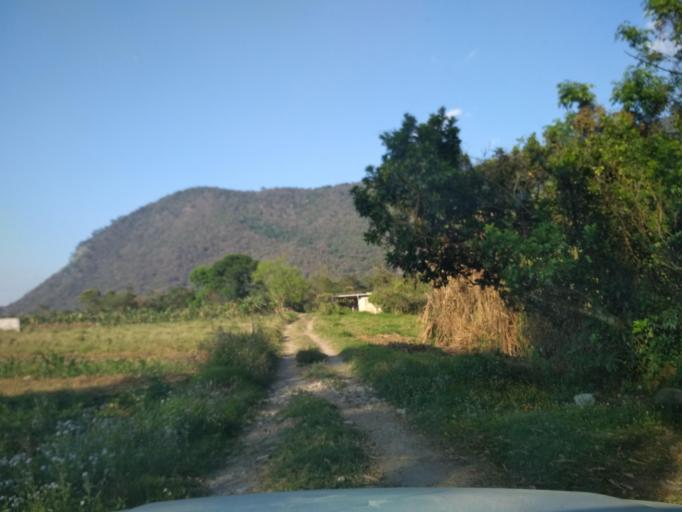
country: MX
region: Veracruz
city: Jalapilla
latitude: 18.8174
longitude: -97.0733
